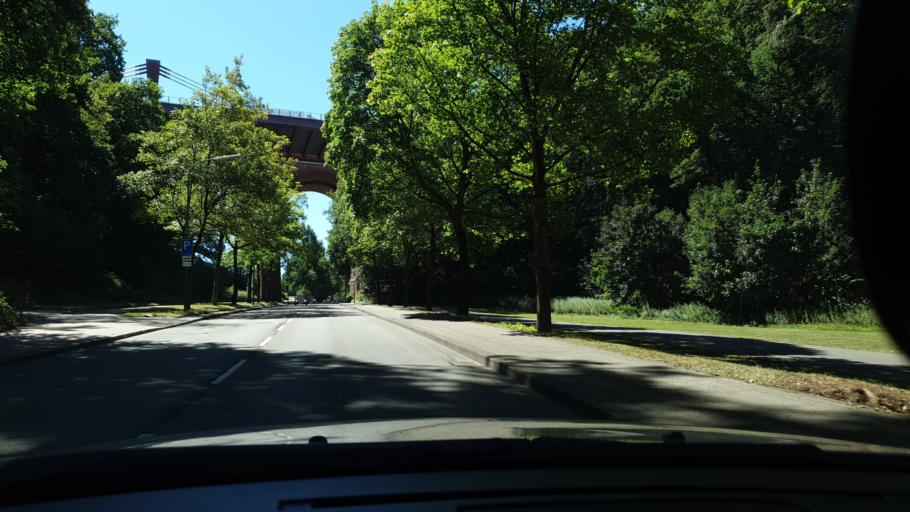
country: DE
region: Rheinland-Pfalz
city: Kaiserslautern
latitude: 49.4583
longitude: 7.7611
